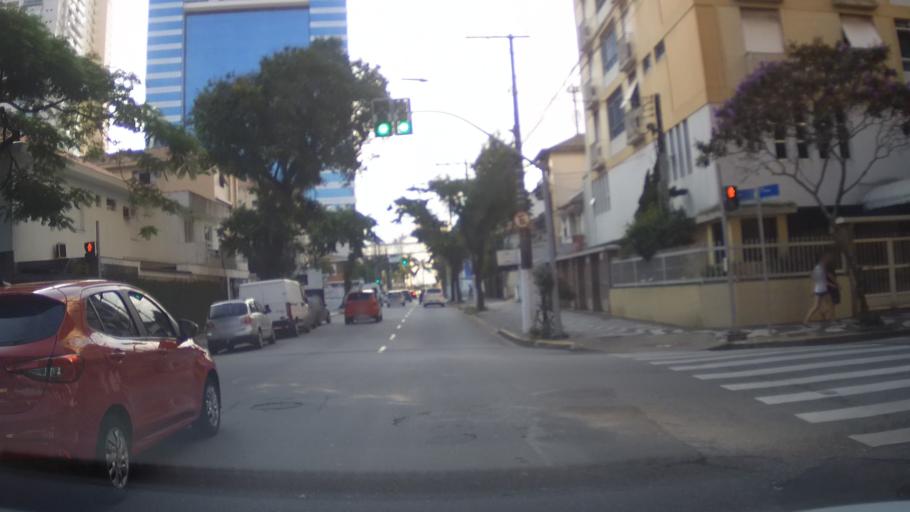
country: BR
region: Sao Paulo
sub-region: Santos
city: Santos
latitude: -23.9801
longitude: -46.3071
